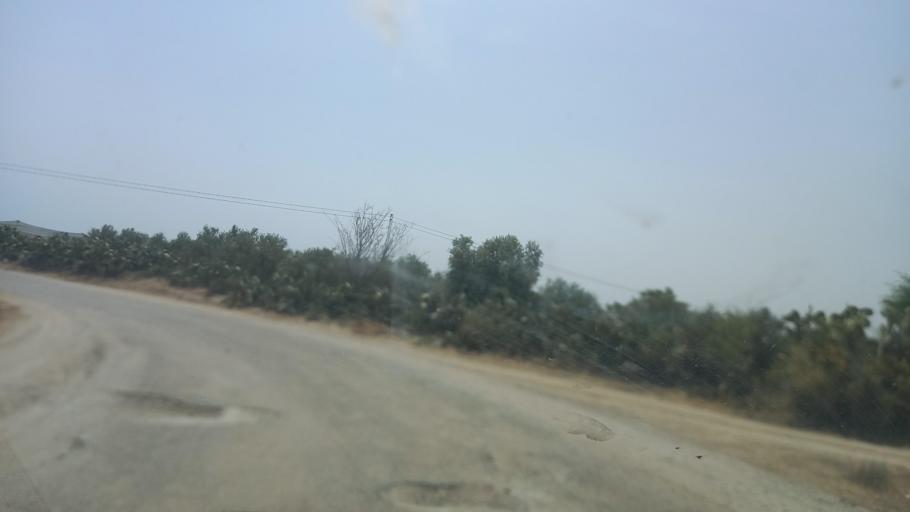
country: TN
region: Al Qasrayn
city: Kasserine
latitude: 35.2468
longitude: 9.0287
